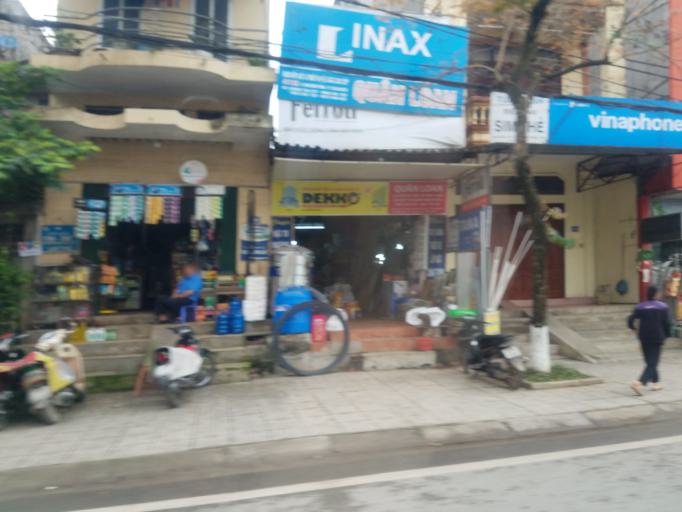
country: VN
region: Thai Nguyen
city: Thanh Pho Thai Nguyen
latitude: 21.5826
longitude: 105.8382
